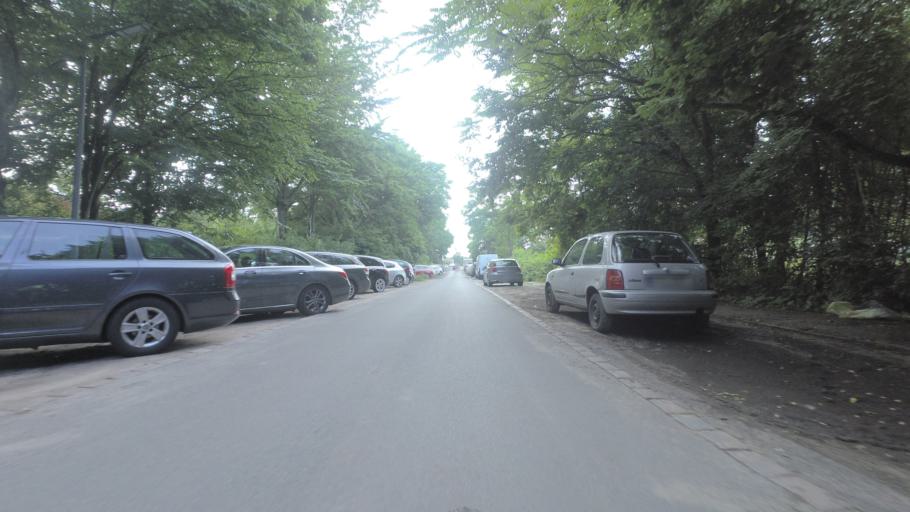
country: DE
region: Berlin
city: Rudow
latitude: 52.4046
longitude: 13.4926
